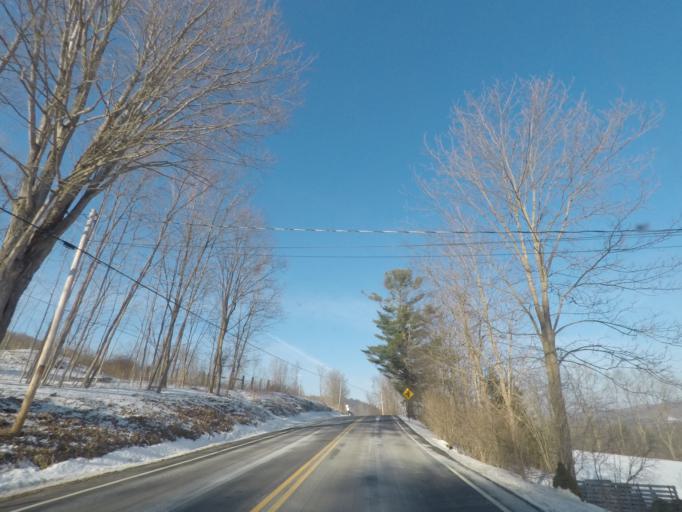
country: US
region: Massachusetts
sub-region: Berkshire County
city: Richmond
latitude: 42.4904
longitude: -73.3876
